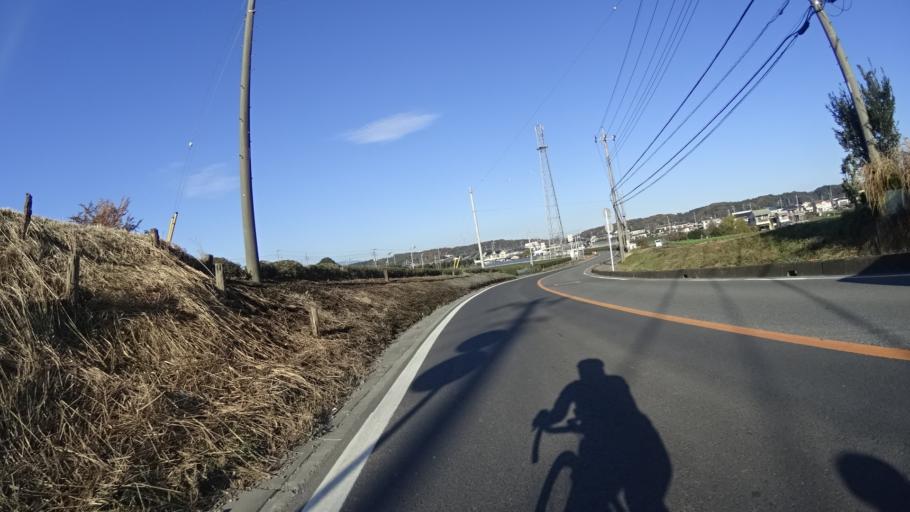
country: JP
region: Saitama
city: Hanno
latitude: 35.8092
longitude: 139.3330
